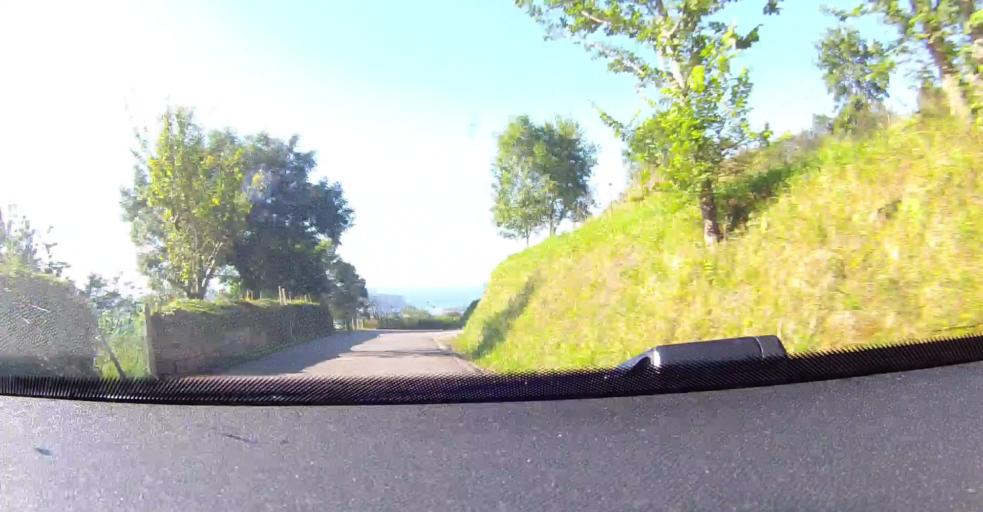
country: ES
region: Asturias
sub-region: Province of Asturias
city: Villaviciosa
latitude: 43.4875
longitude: -5.3919
